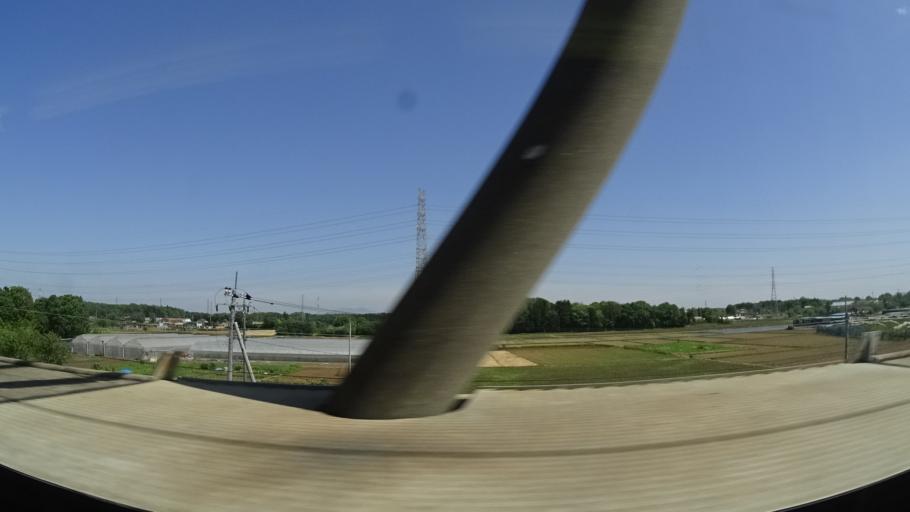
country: JP
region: Tochigi
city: Oyama
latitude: 36.3571
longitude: 139.8320
